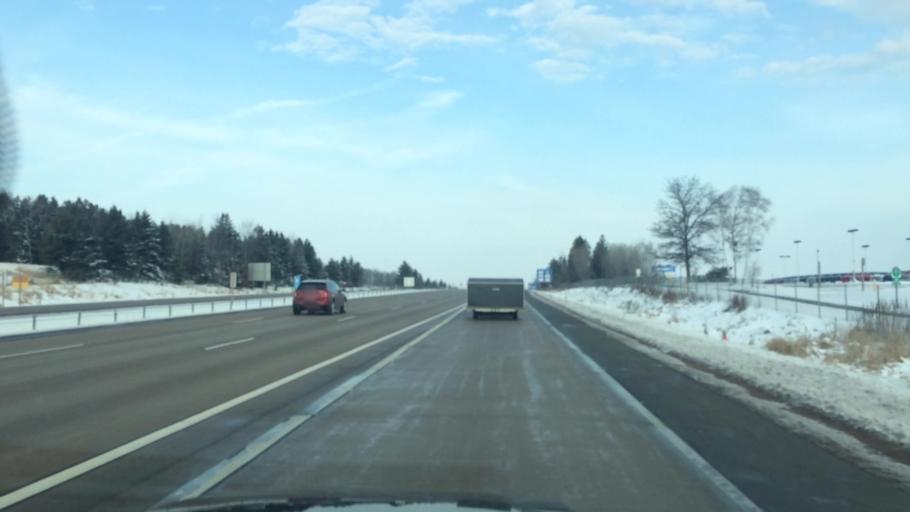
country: US
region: Wisconsin
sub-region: Marathon County
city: Rib Mountain
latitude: 44.9154
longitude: -89.6532
